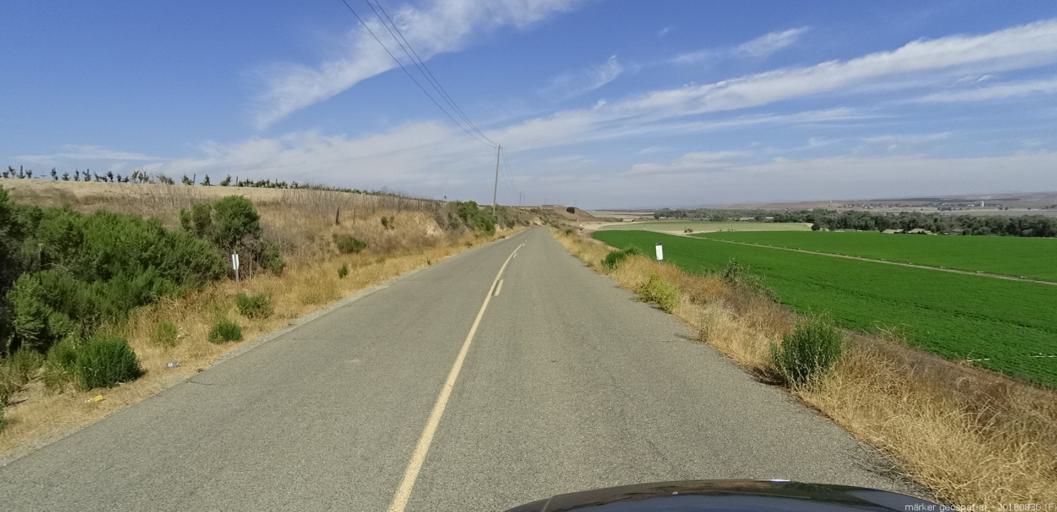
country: US
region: California
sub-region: Monterey County
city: King City
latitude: 36.0972
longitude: -121.0203
